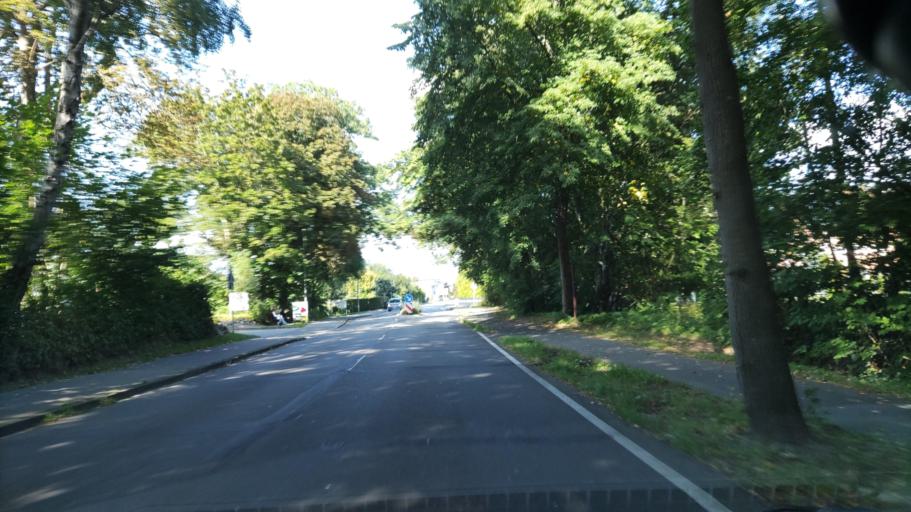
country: DE
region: Schleswig-Holstein
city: Aukrug
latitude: 54.0796
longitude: 9.7787
